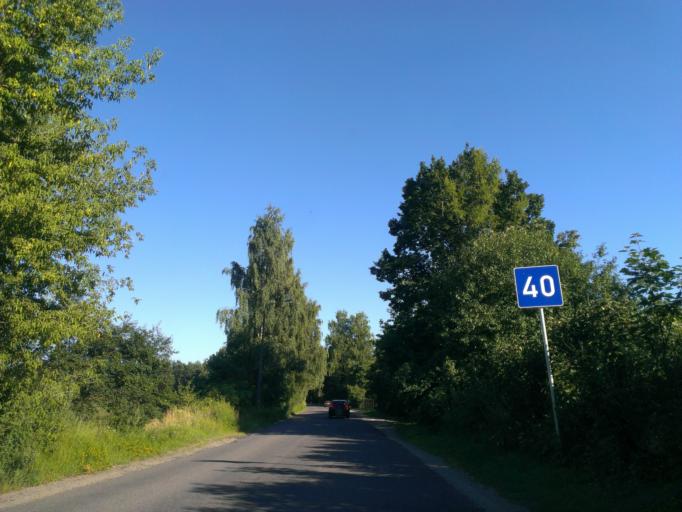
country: LV
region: Riga
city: Bergi
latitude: 56.9963
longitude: 24.2789
